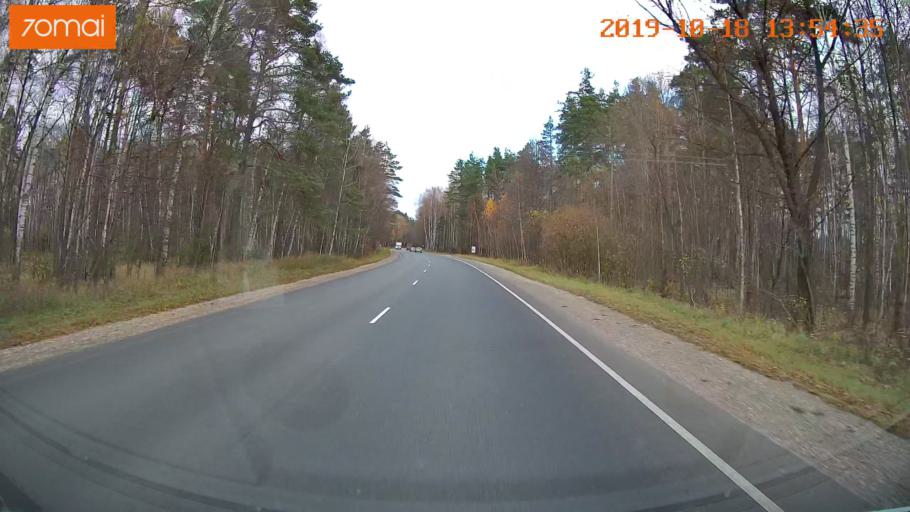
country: RU
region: Rjazan
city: Spas-Klepiki
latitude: 55.0440
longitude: 40.0112
